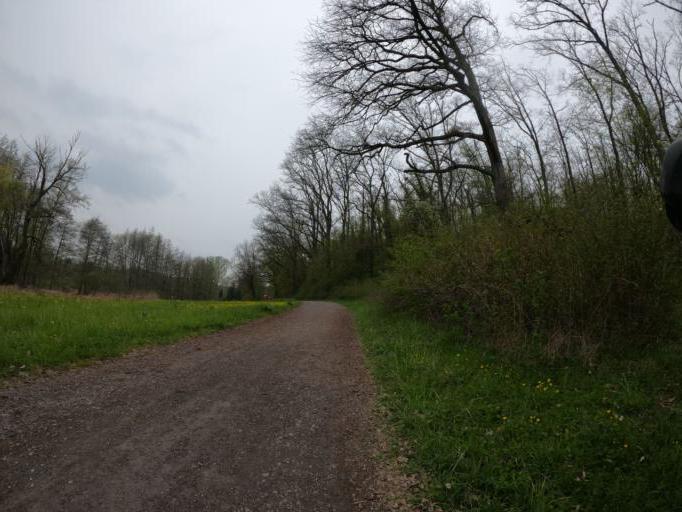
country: DE
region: Baden-Wuerttemberg
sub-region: Karlsruhe Region
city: Illingen
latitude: 48.9680
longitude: 8.9138
